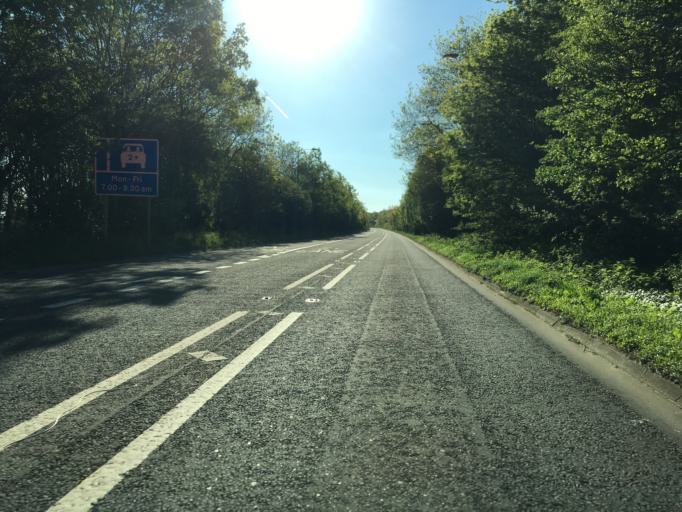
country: GB
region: England
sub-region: North Somerset
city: Long Ashton
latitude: 51.4195
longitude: -2.6820
